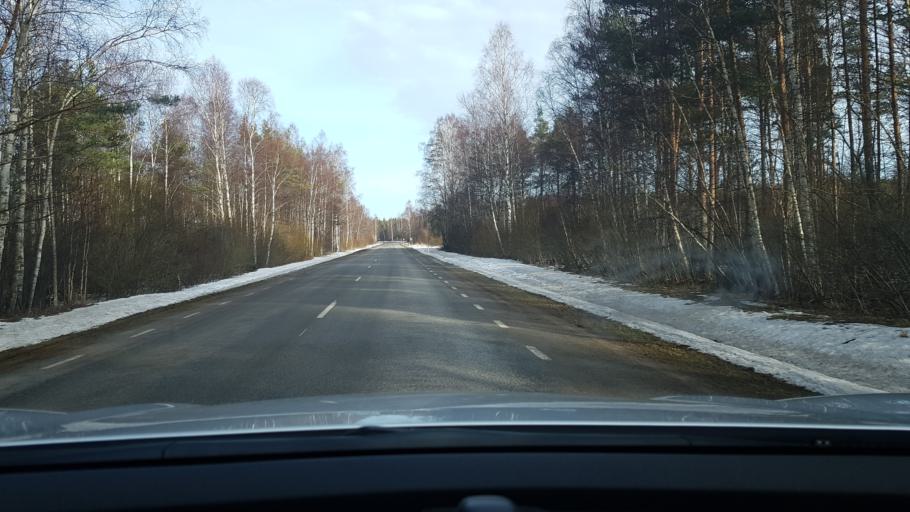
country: EE
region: Saare
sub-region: Kuressaare linn
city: Kuressaare
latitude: 58.4846
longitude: 22.7068
